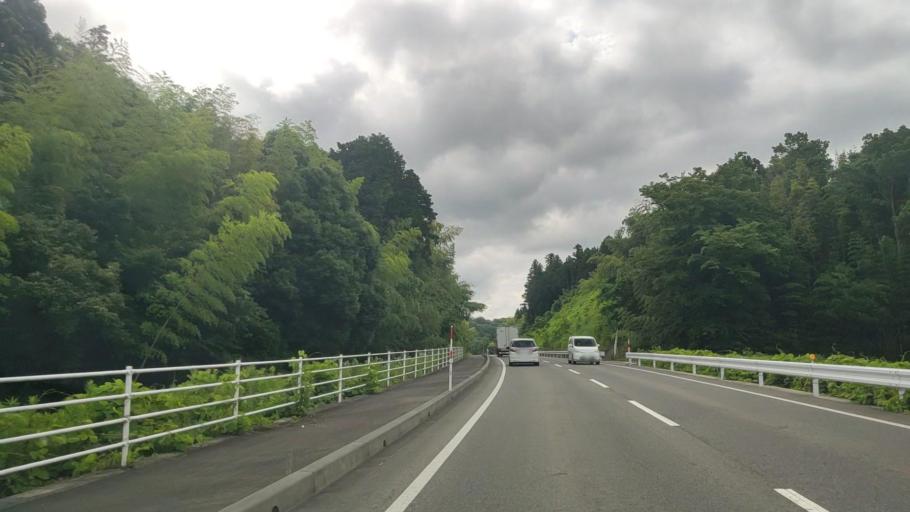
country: JP
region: Tottori
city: Yonago
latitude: 35.3795
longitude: 133.3900
